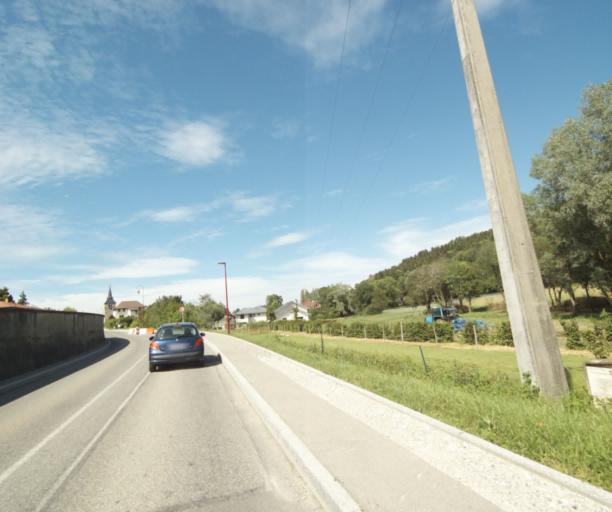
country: FR
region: Rhone-Alpes
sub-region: Departement de la Haute-Savoie
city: Perrignier
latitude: 46.3008
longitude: 6.4571
